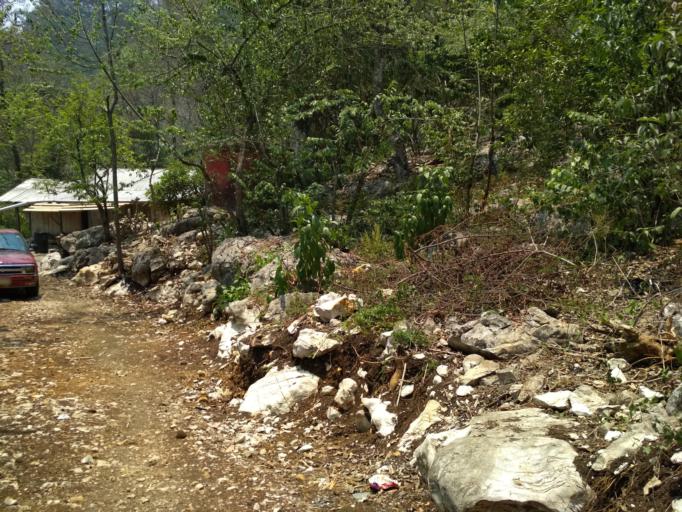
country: MX
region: Veracruz
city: Cosolapa
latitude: 18.6013
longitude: -96.7253
